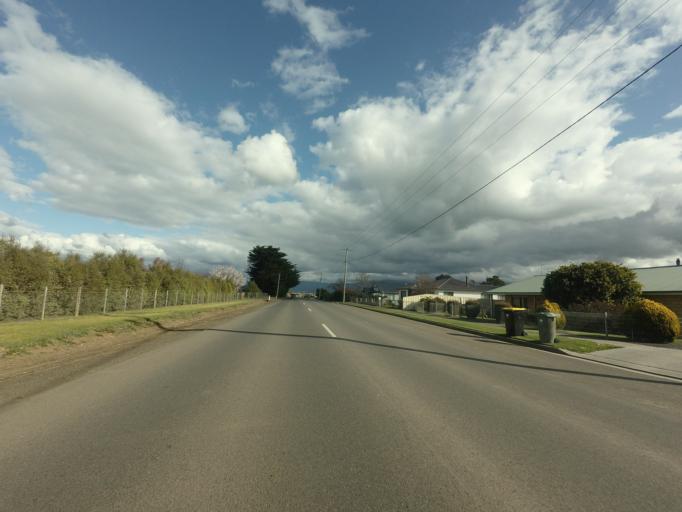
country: AU
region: Tasmania
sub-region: Northern Midlands
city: Longford
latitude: -41.6949
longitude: 147.0784
